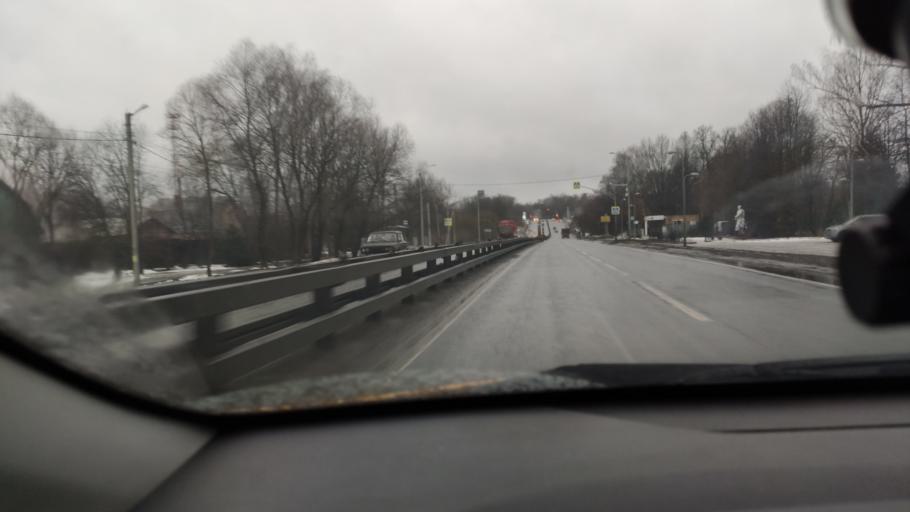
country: RU
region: Moskovskaya
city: Troitsk
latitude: 55.3023
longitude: 37.2121
